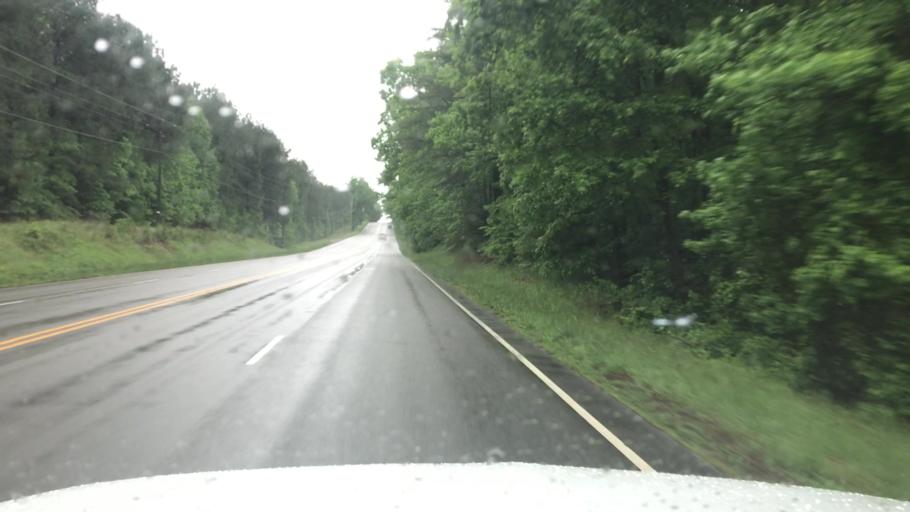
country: US
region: Virginia
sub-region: Hanover County
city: Ashland
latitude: 37.8372
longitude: -77.4676
